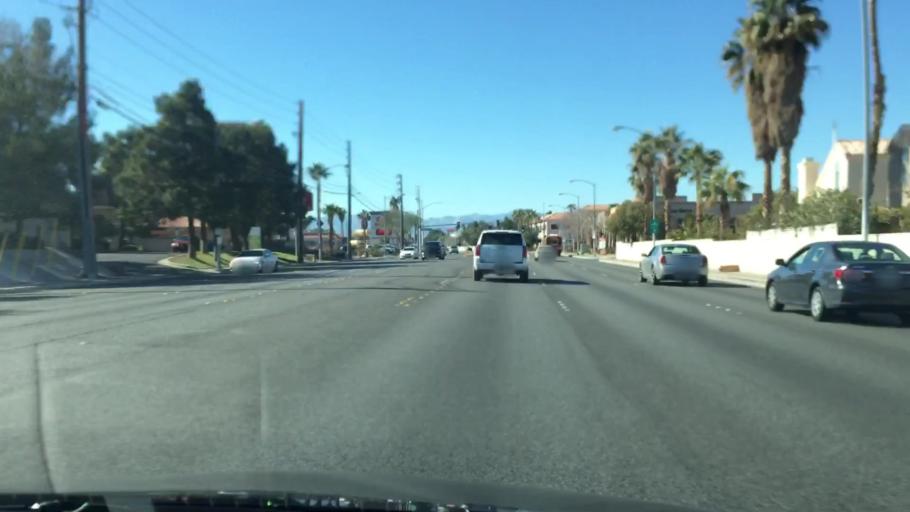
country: US
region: Nevada
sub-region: Clark County
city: Whitney
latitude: 36.0577
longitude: -115.1252
